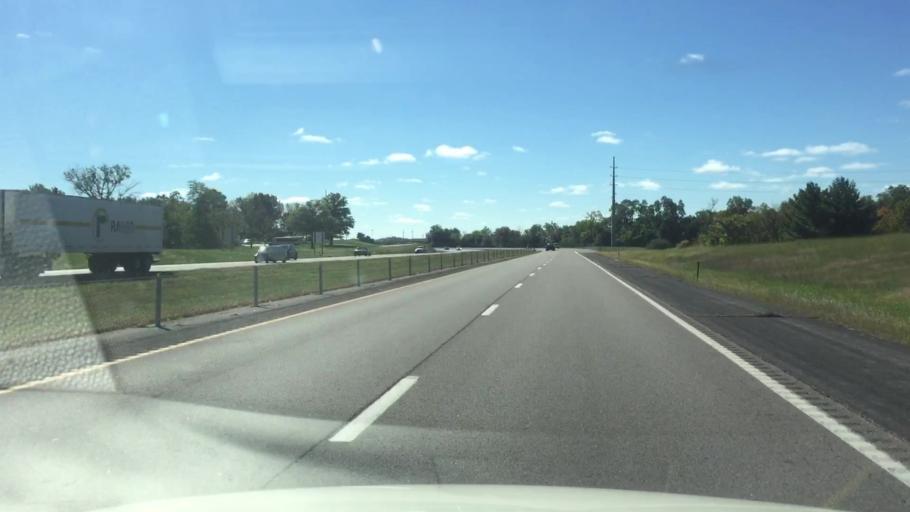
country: US
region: Missouri
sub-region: Boone County
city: Columbia
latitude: 38.9121
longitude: -92.2938
